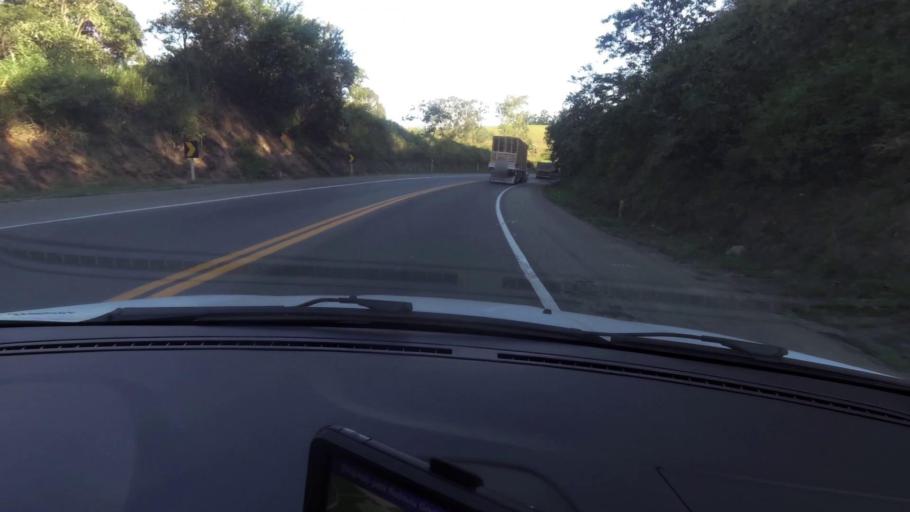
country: BR
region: Espirito Santo
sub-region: Alfredo Chaves
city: Alfredo Chaves
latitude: -20.6830
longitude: -40.6683
